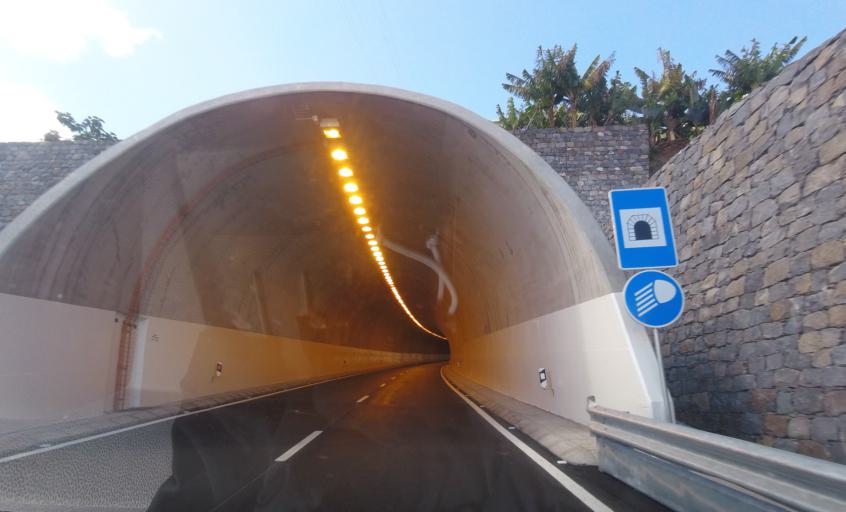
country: PT
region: Madeira
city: Camara de Lobos
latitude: 32.6637
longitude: -16.9690
